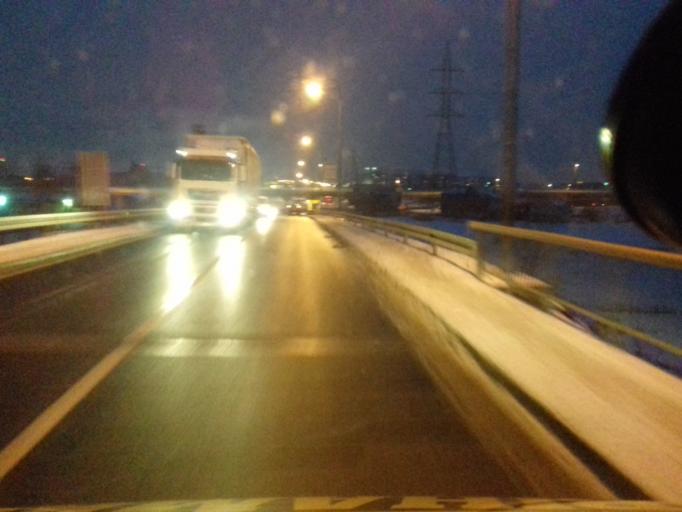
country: BA
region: Federation of Bosnia and Herzegovina
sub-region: Kanton Sarajevo
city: Sarajevo
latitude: 43.8541
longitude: 18.3262
